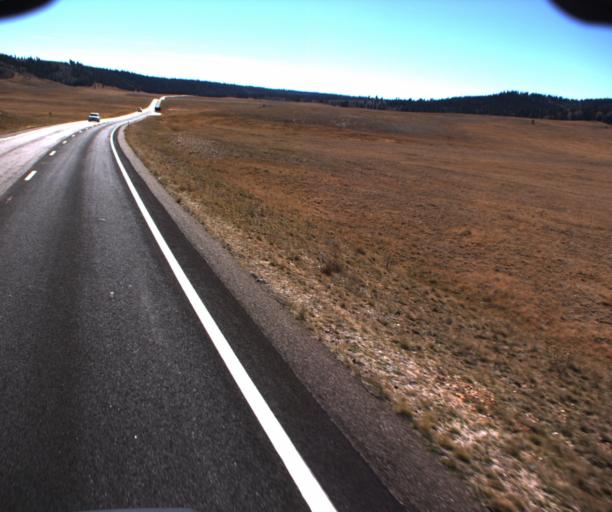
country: US
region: Arizona
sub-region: Coconino County
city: Grand Canyon
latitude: 36.4961
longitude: -112.1326
